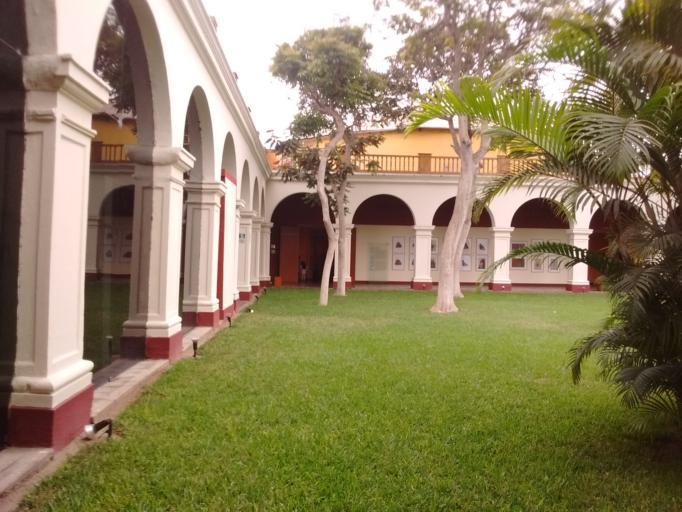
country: PE
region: Lima
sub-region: Lima
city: San Isidro
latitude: -12.0771
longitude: -77.0621
